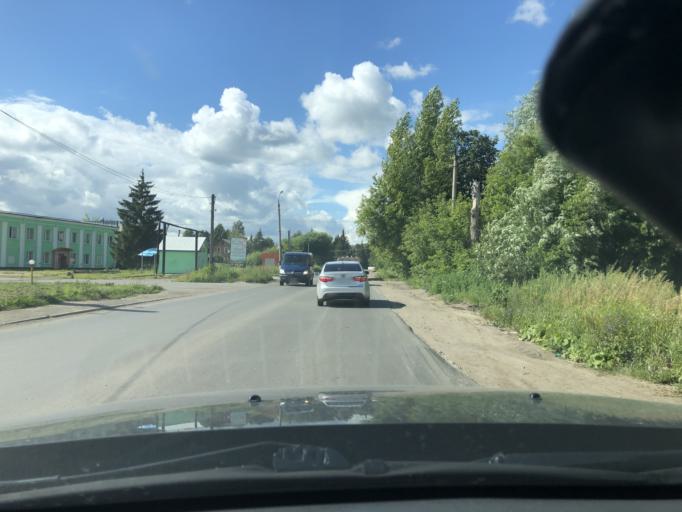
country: RU
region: Tula
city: Donskoy
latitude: 53.9684
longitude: 38.3583
